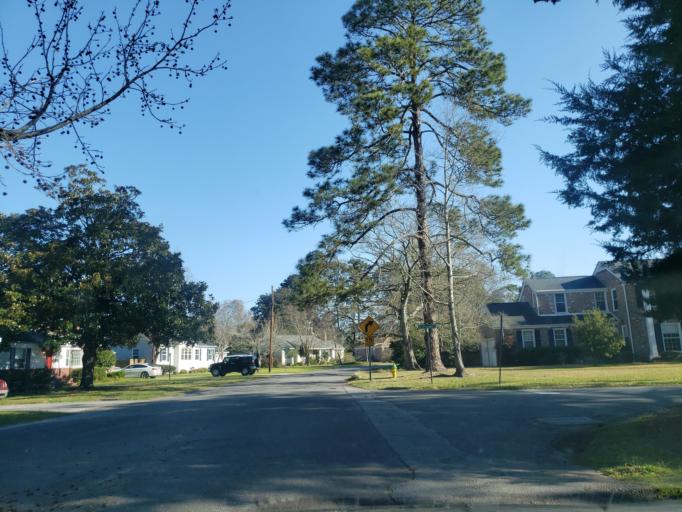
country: US
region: Georgia
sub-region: Chatham County
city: Thunderbolt
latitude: 32.0219
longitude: -81.0931
